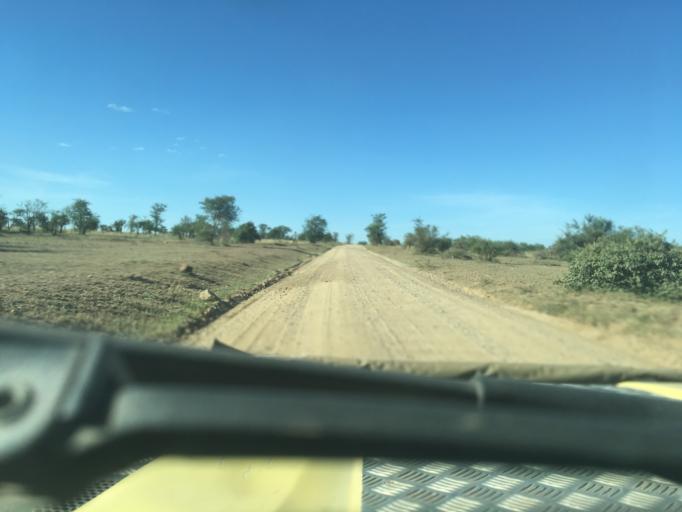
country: TZ
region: Mara
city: Mugumu
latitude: -2.3942
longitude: 34.8131
